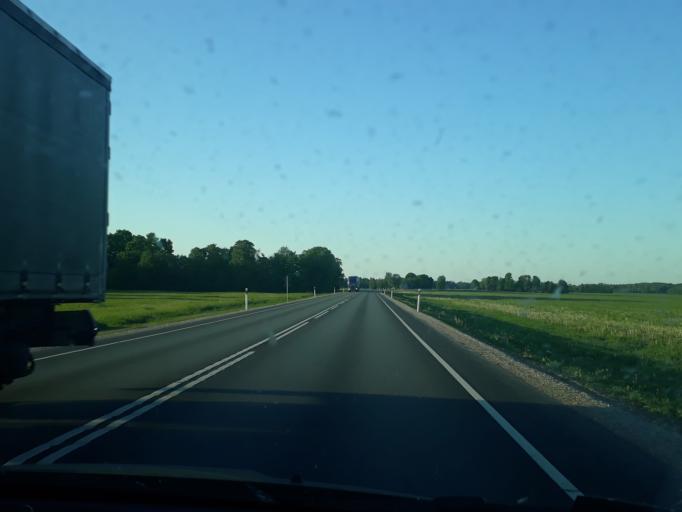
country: EE
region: Paernumaa
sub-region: Tootsi vald
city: Tootsi
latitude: 58.5467
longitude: 24.8471
